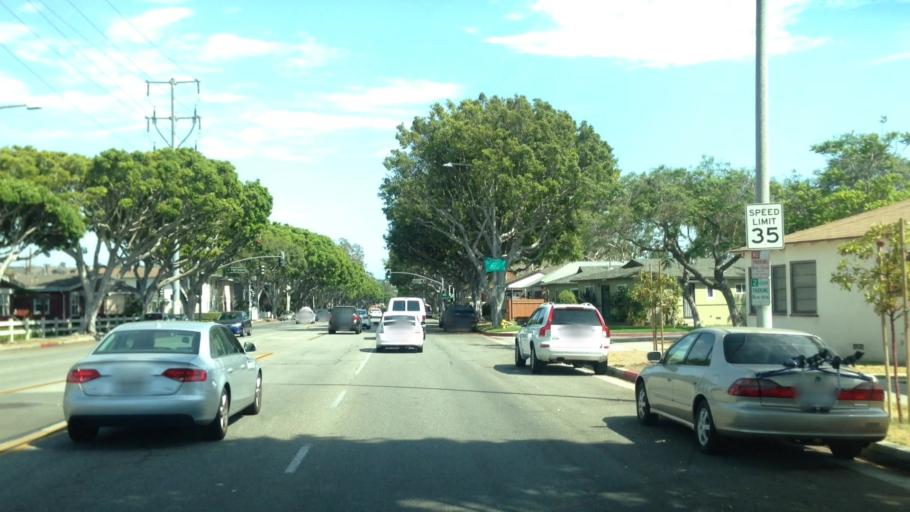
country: US
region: California
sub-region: Los Angeles County
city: Culver City
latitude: 34.0112
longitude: -118.4001
